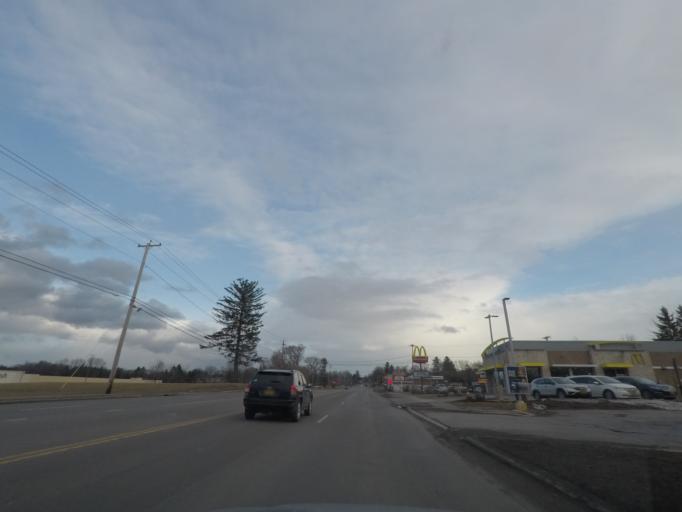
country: US
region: New York
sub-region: Oneida County
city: New Hartford
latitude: 43.0802
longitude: -75.3189
